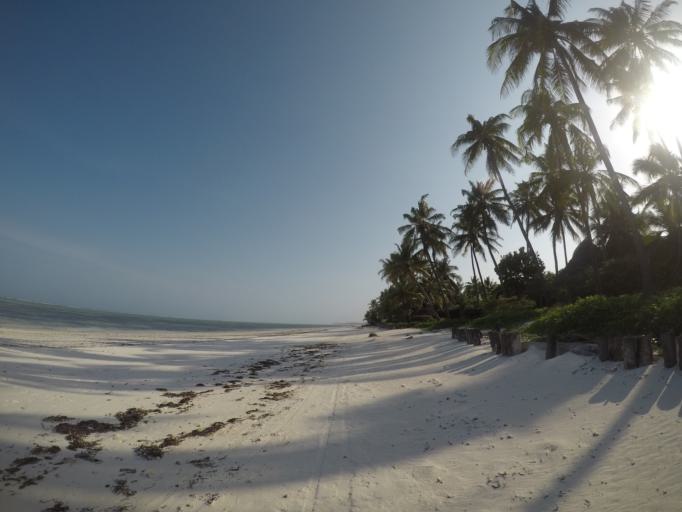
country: TZ
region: Zanzibar Central/South
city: Nganane
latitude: -6.2023
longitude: 39.5351
